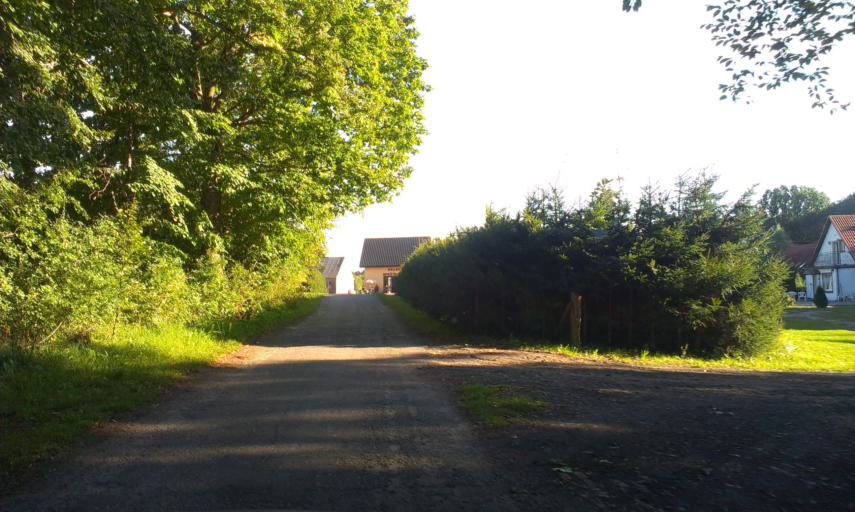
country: PL
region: West Pomeranian Voivodeship
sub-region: Powiat szczecinecki
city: Szczecinek
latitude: 53.8455
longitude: 16.6757
